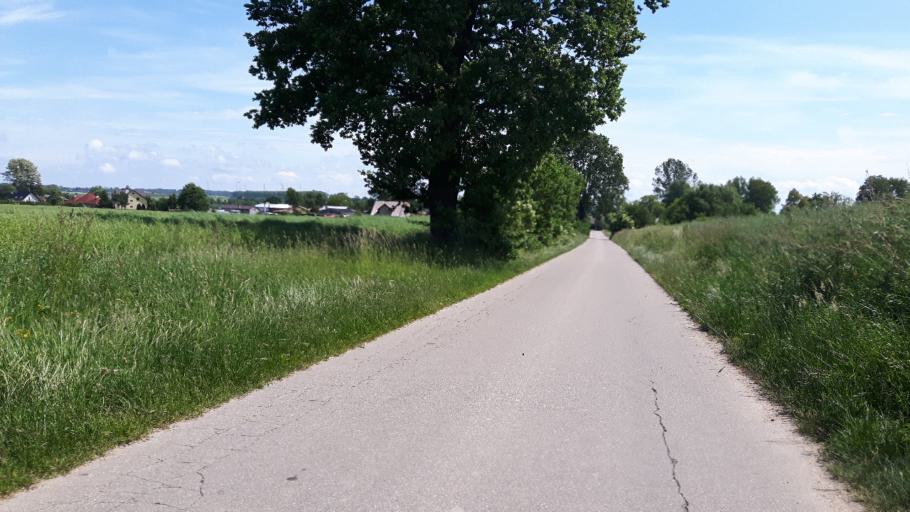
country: PL
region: Pomeranian Voivodeship
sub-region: Powiat wejherowski
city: Gniewino
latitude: 54.7254
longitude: 17.9591
